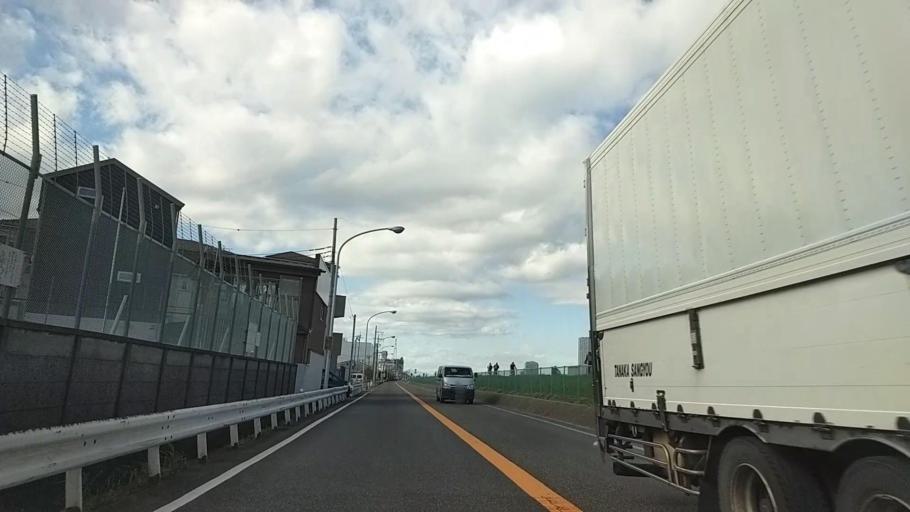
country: JP
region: Kanagawa
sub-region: Kawasaki-shi
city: Kawasaki
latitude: 35.5940
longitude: 139.6451
